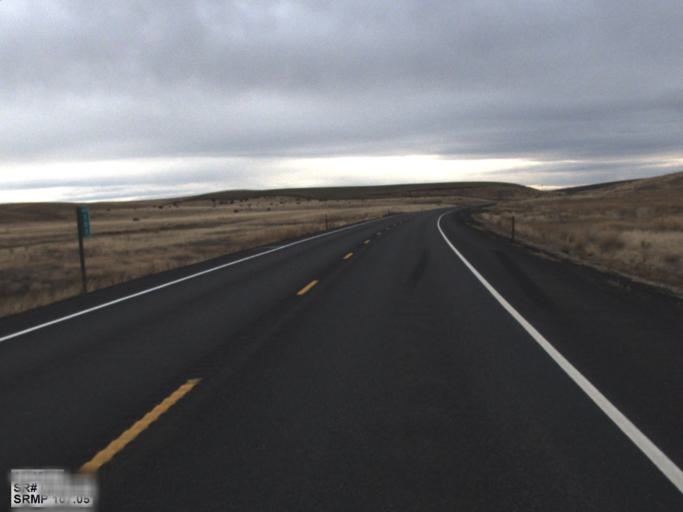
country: US
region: Washington
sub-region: Garfield County
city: Pomeroy
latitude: 46.7999
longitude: -117.8493
